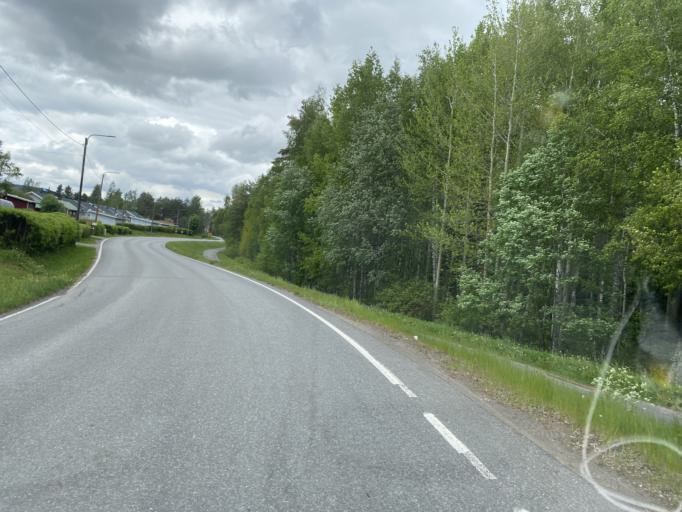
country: FI
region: Pirkanmaa
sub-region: Etelae-Pirkanmaa
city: Urjala
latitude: 61.0769
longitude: 23.5666
